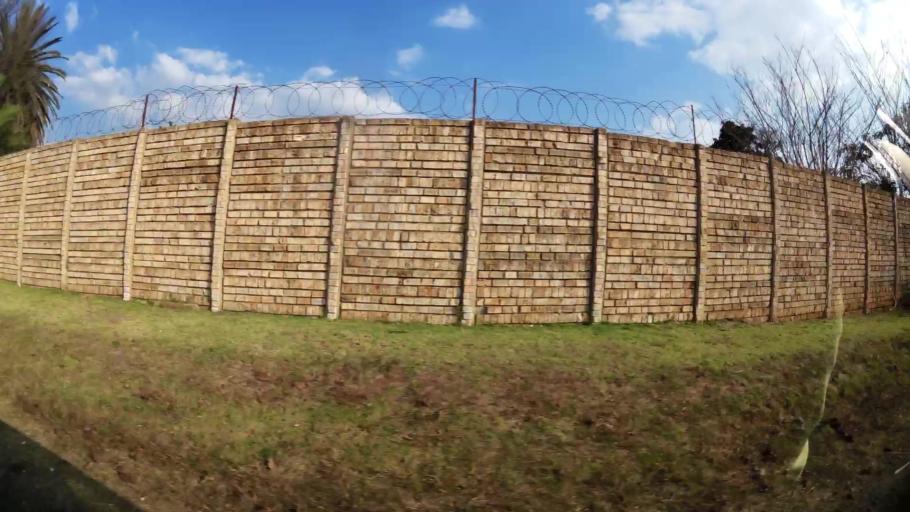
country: ZA
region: Gauteng
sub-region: Ekurhuleni Metropolitan Municipality
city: Benoni
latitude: -26.1009
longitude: 28.2773
